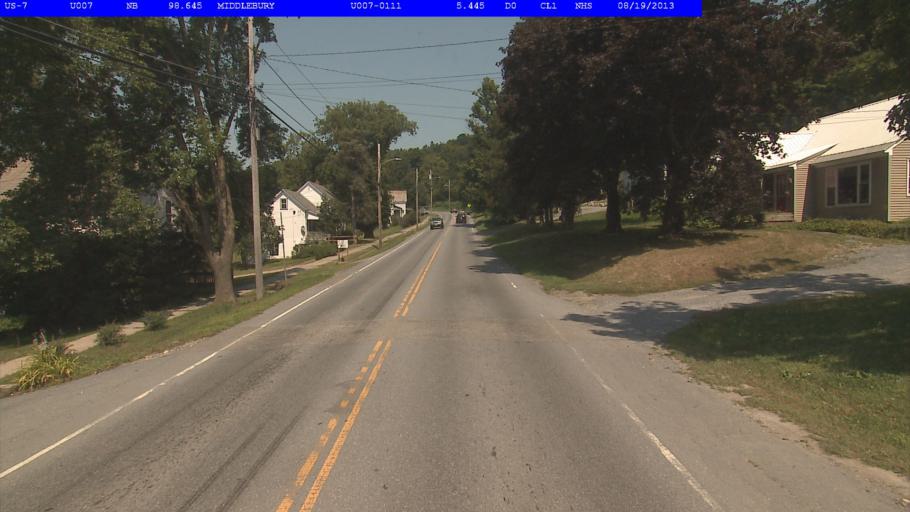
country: US
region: Vermont
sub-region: Addison County
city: Middlebury (village)
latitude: 44.0193
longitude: -73.1660
